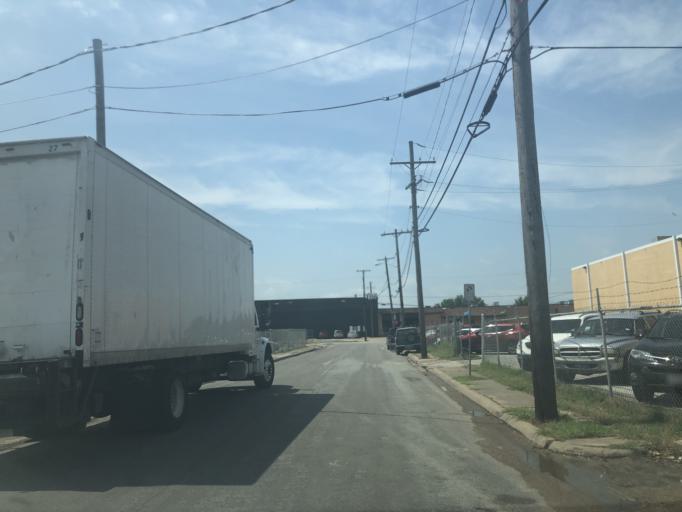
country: US
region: Texas
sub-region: Dallas County
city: Dallas
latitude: 32.8048
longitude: -96.8672
